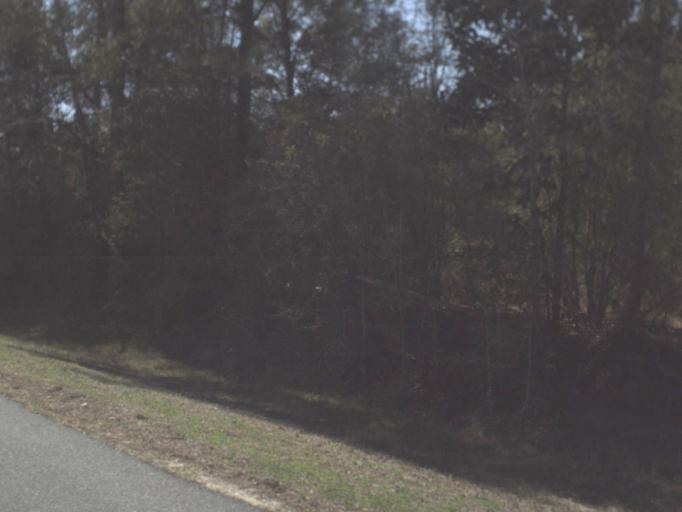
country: US
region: Florida
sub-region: Jackson County
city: Sneads
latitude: 30.6101
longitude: -85.0300
